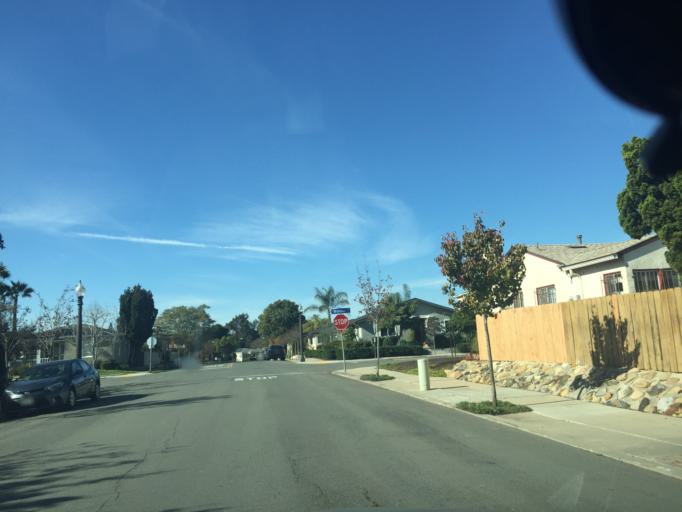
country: US
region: California
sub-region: San Diego County
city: Lemon Grove
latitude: 32.7629
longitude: -117.0874
